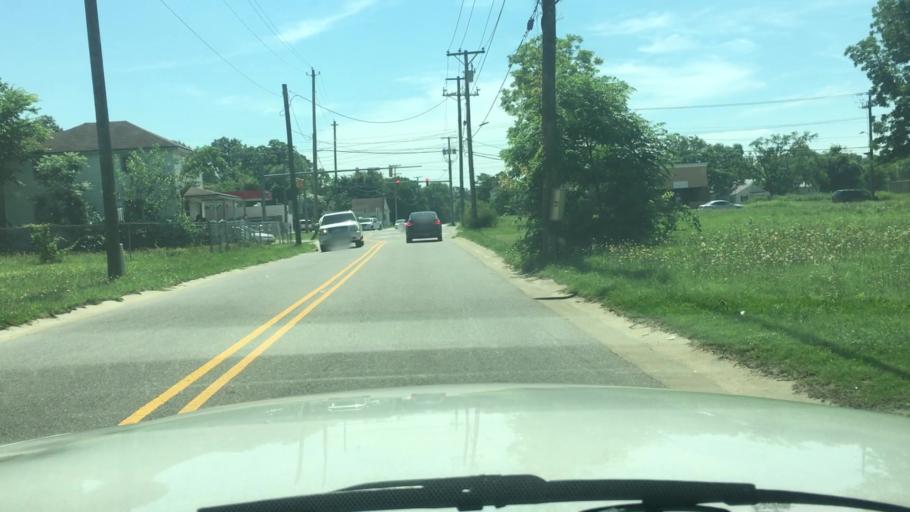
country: US
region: North Carolina
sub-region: Cumberland County
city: Fayetteville
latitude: 35.0465
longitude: -78.8815
